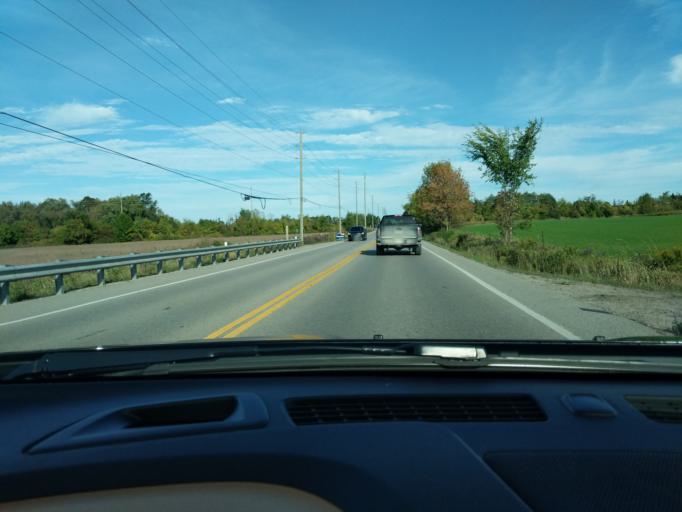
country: CA
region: Ontario
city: Collingwood
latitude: 44.4816
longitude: -80.1999
